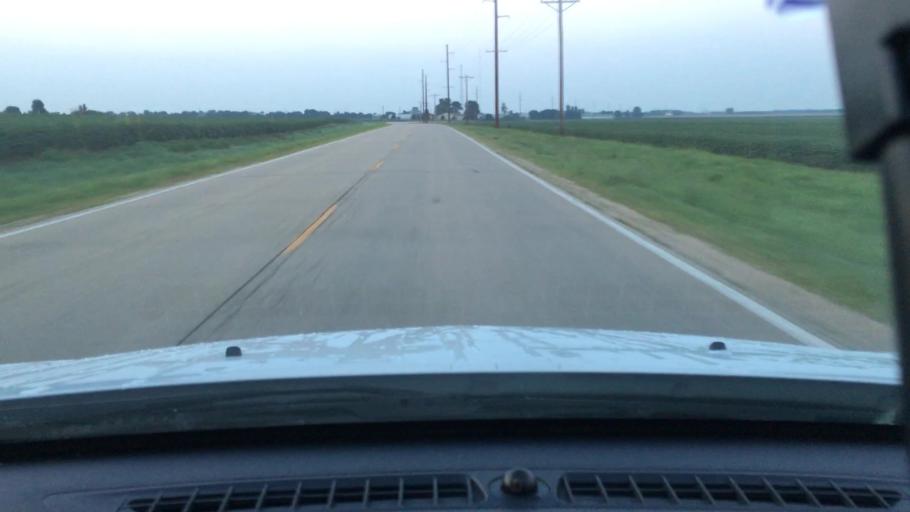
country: US
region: Illinois
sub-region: Ogle County
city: Rochelle
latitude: 41.8878
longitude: -89.0273
